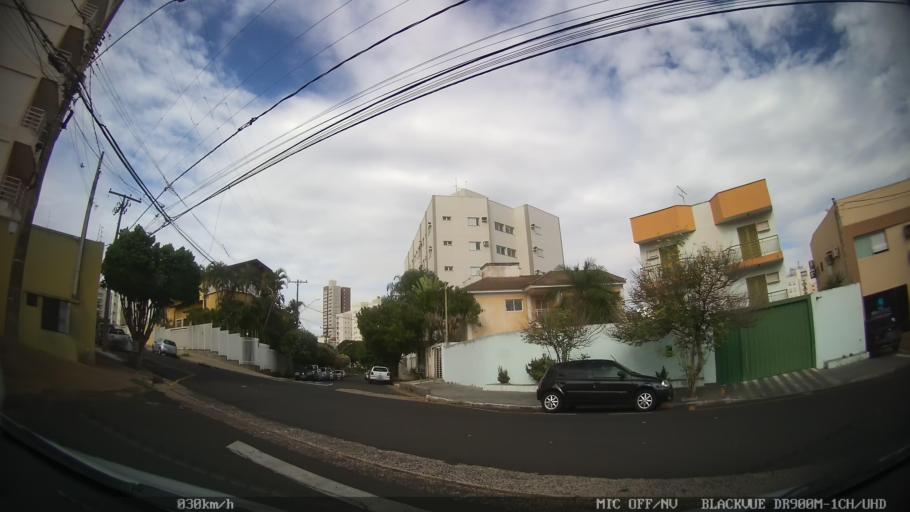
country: BR
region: Sao Paulo
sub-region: Sao Jose Do Rio Preto
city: Sao Jose do Rio Preto
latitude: -20.8311
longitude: -49.3843
